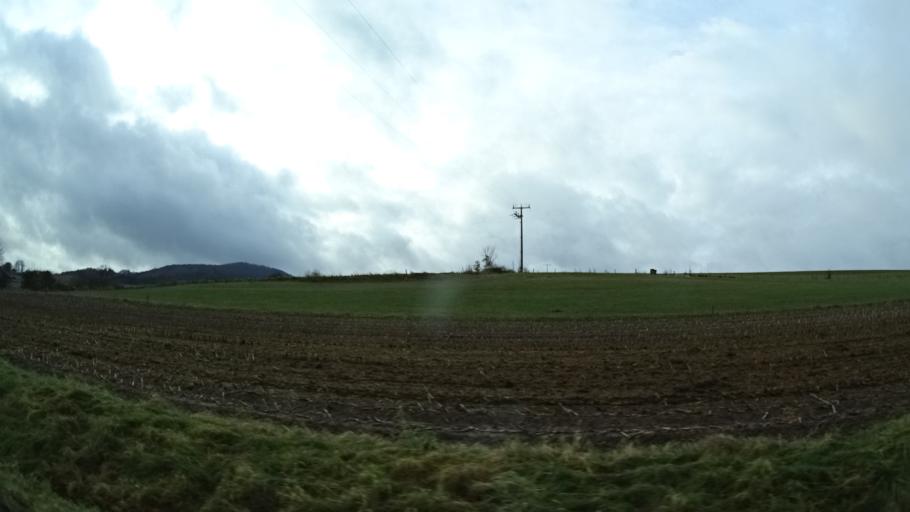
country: DE
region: Hesse
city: Tann
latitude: 50.6182
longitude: 10.0295
